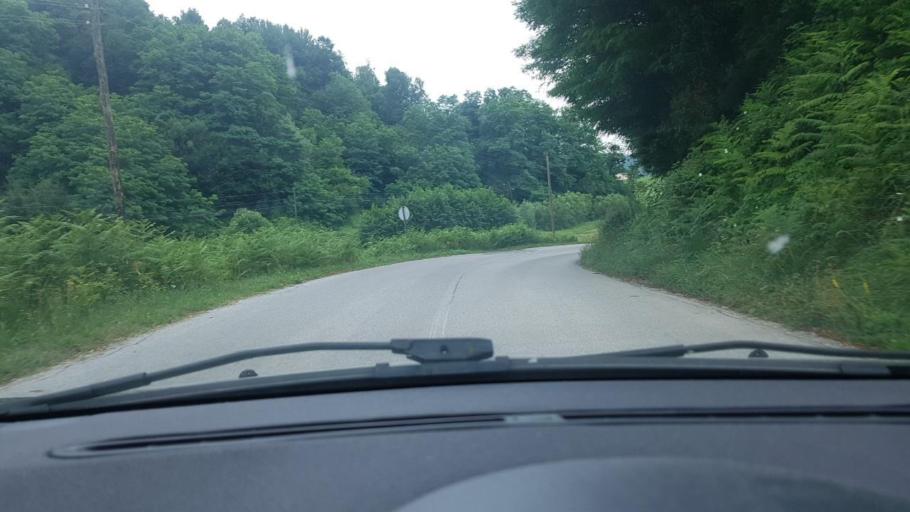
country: SI
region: Podlehnik
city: Podlehnik
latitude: 46.2880
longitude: 15.9574
